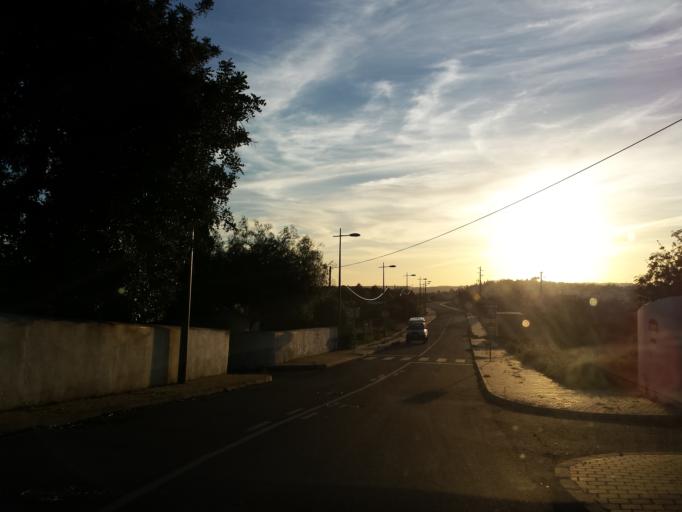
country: PT
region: Faro
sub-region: Lagos
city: Lagos
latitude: 37.1268
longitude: -8.6494
